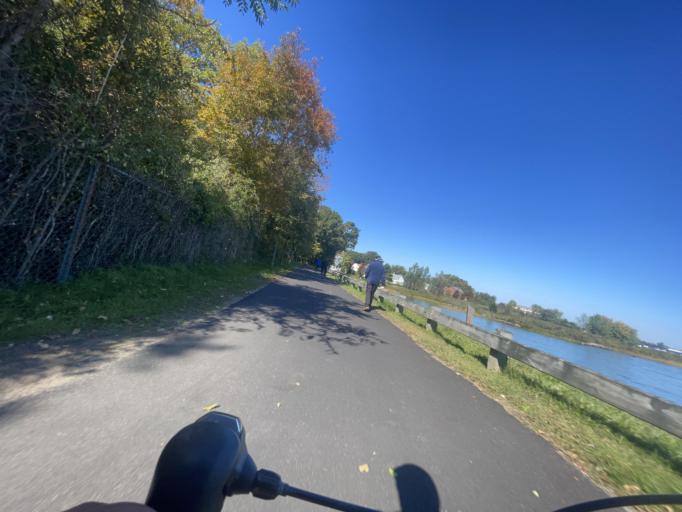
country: US
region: Massachusetts
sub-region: Norfolk County
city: Milton
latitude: 42.2862
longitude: -71.0387
